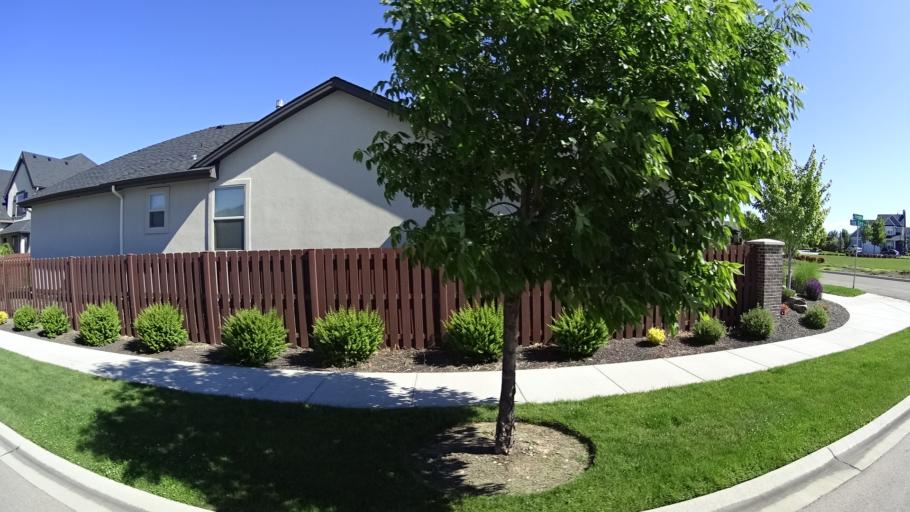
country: US
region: Idaho
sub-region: Ada County
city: Meridian
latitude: 43.6680
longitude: -116.4079
